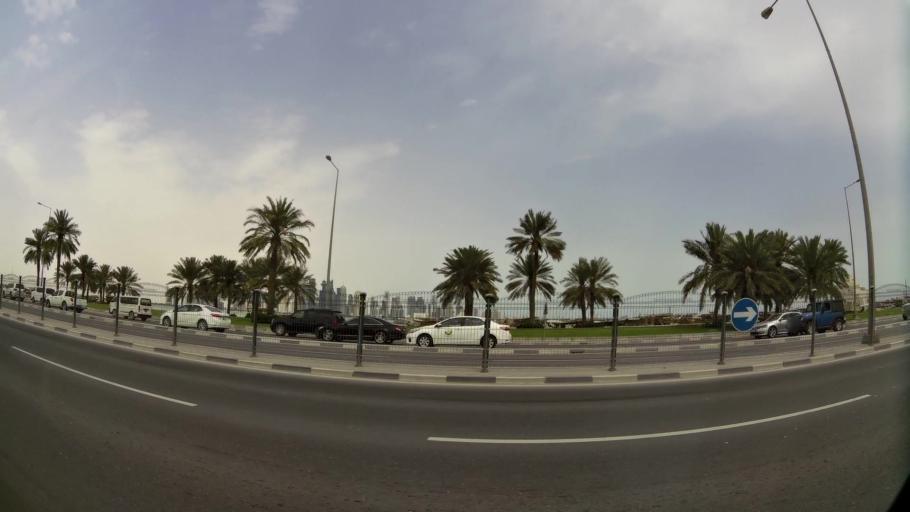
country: QA
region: Baladiyat ad Dawhah
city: Doha
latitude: 25.2914
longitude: 51.5315
